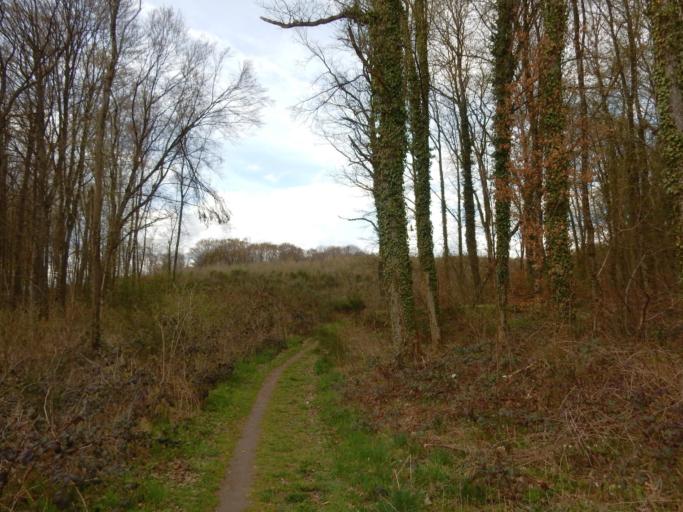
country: LU
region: Luxembourg
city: Eischen
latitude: 49.6732
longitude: 5.8826
